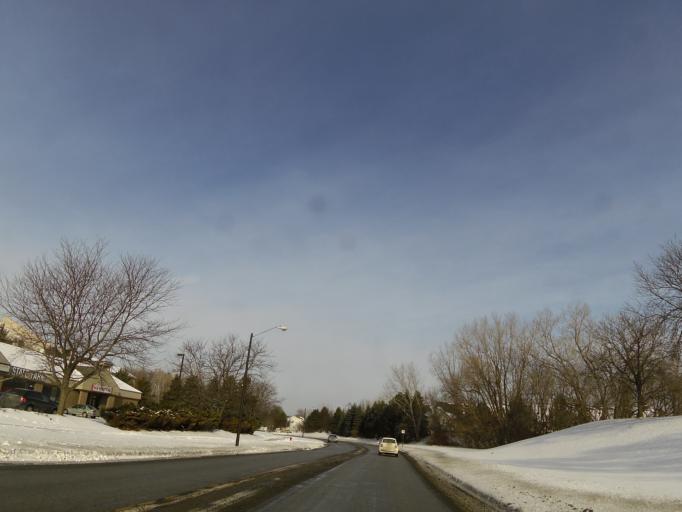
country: US
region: Minnesota
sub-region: Hennepin County
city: Eden Prairie
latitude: 44.8523
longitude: -93.4543
